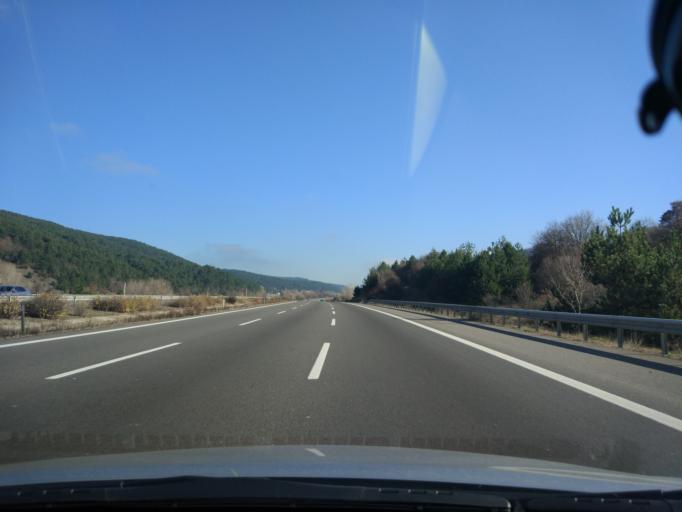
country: TR
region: Bolu
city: Gokcesu
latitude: 40.7396
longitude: 31.8368
